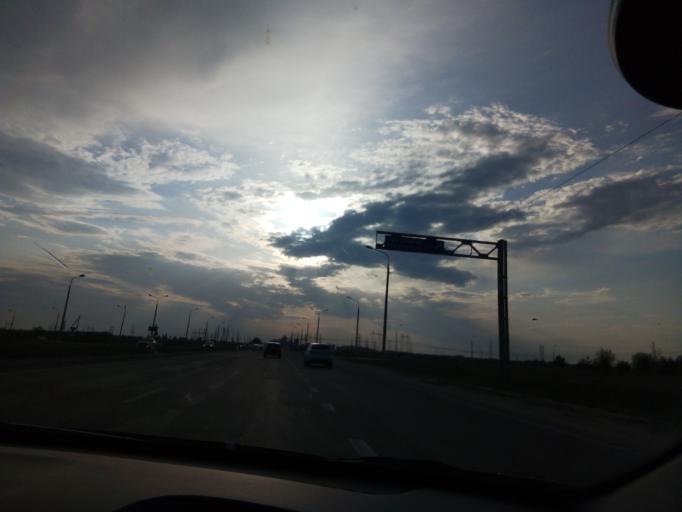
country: RU
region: Chuvashia
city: Novocheboksarsk
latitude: 56.1217
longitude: 47.4317
